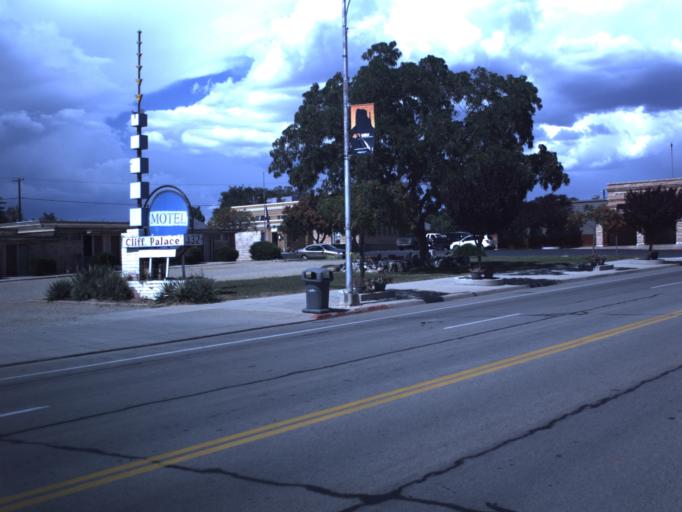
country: US
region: Utah
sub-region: San Juan County
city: Blanding
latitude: 37.6233
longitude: -109.4780
